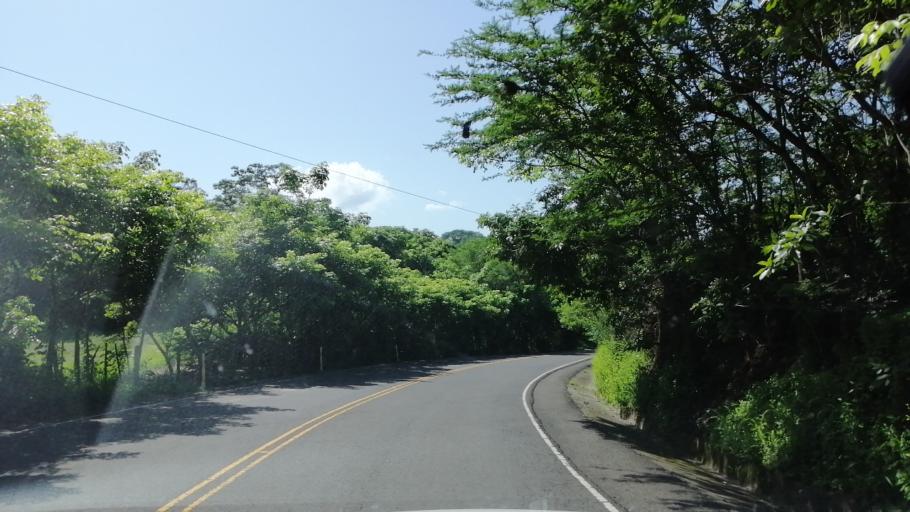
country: HN
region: Lempira
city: La Virtud
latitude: 13.9582
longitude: -88.7542
